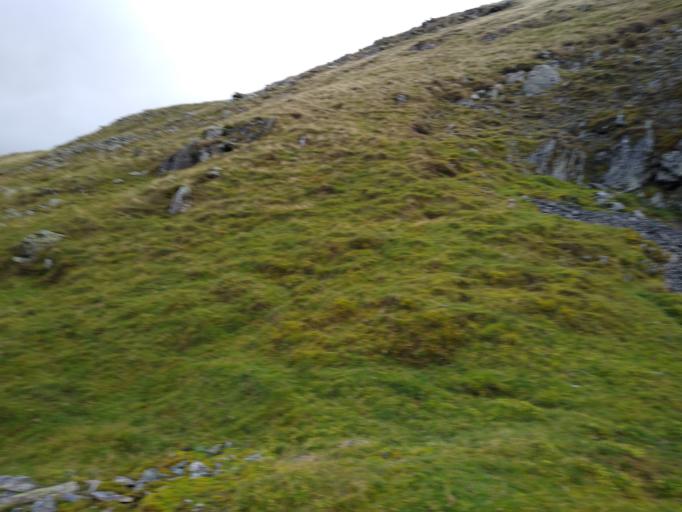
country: GB
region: England
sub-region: Cumbria
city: Ambleside
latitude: 54.4883
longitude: -2.9170
